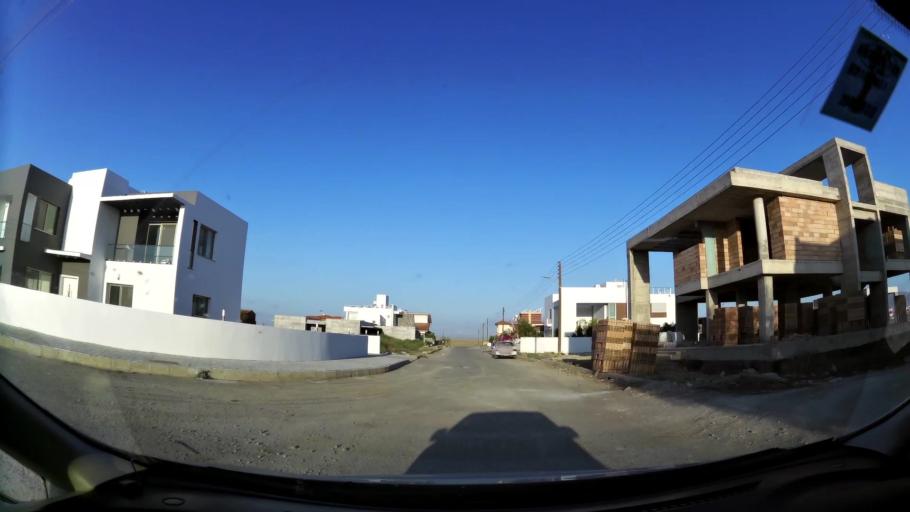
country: CY
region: Lefkosia
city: Nicosia
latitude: 35.1957
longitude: 33.3146
